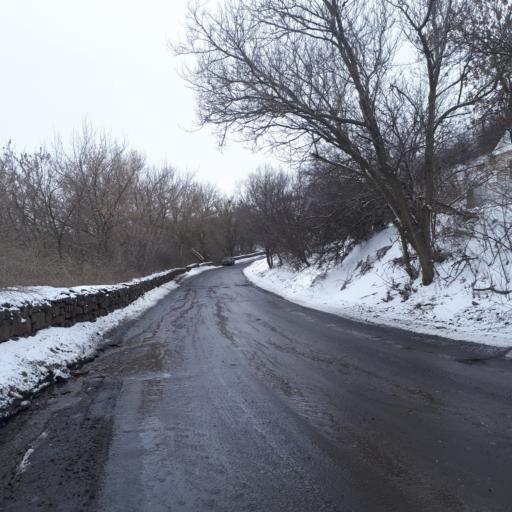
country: RU
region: Rostov
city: Krasnyy Sulin
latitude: 47.9012
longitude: 40.0476
